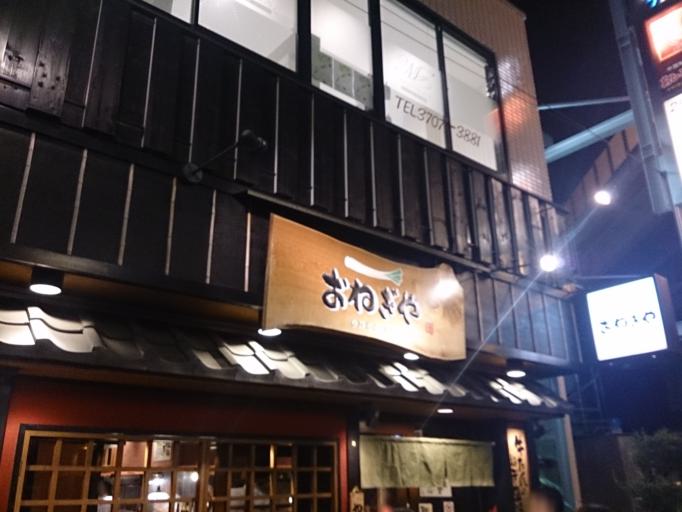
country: JP
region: Tokyo
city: Chofugaoka
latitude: 35.6141
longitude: 139.6252
